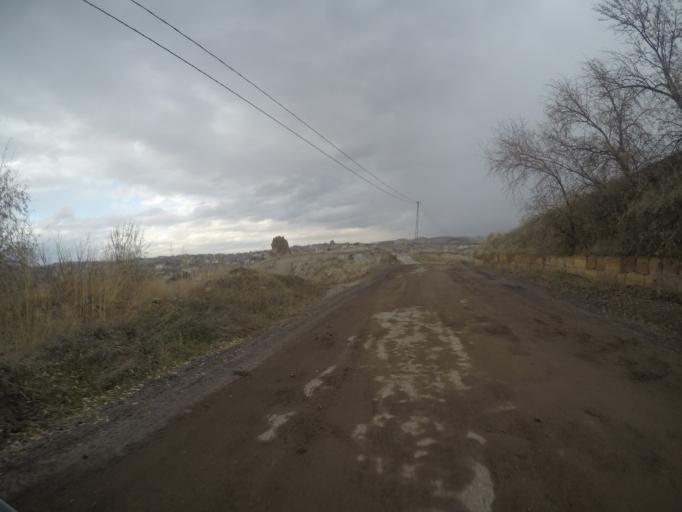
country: TR
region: Nevsehir
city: Goereme
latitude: 38.6155
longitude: 34.8668
